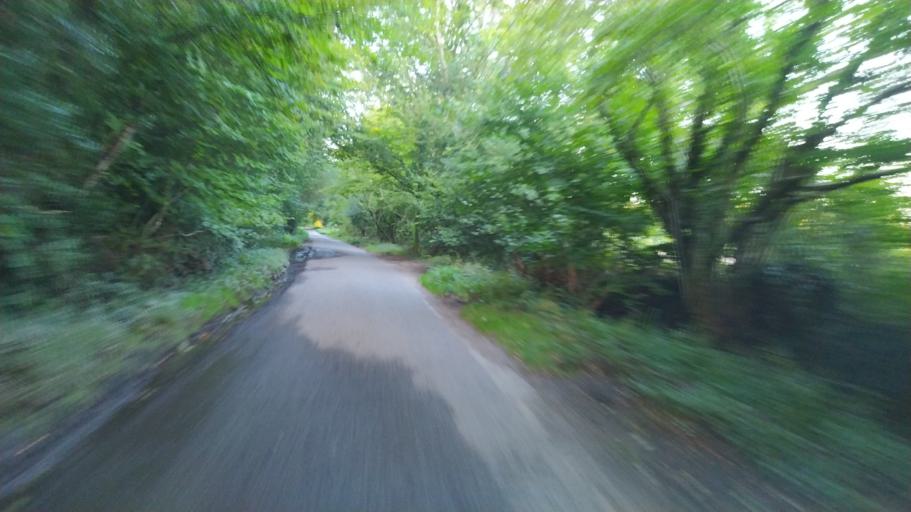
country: GB
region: England
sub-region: Hampshire
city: Lyndhurst
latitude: 50.8656
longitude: -1.5826
